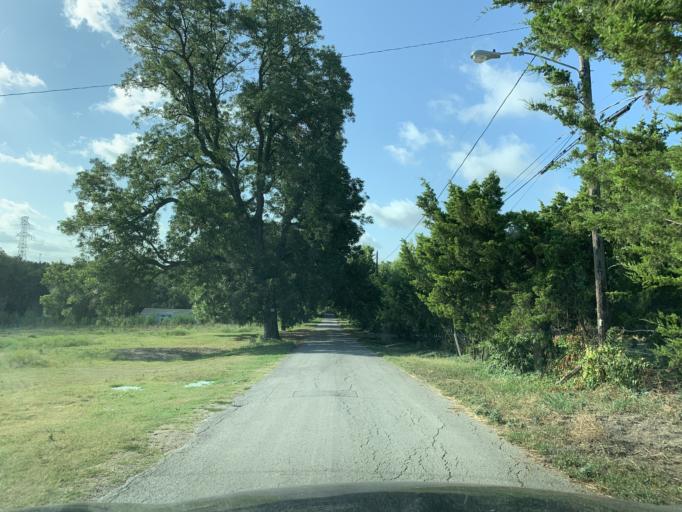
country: US
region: Texas
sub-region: Dallas County
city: Hutchins
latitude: 32.6773
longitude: -96.7737
